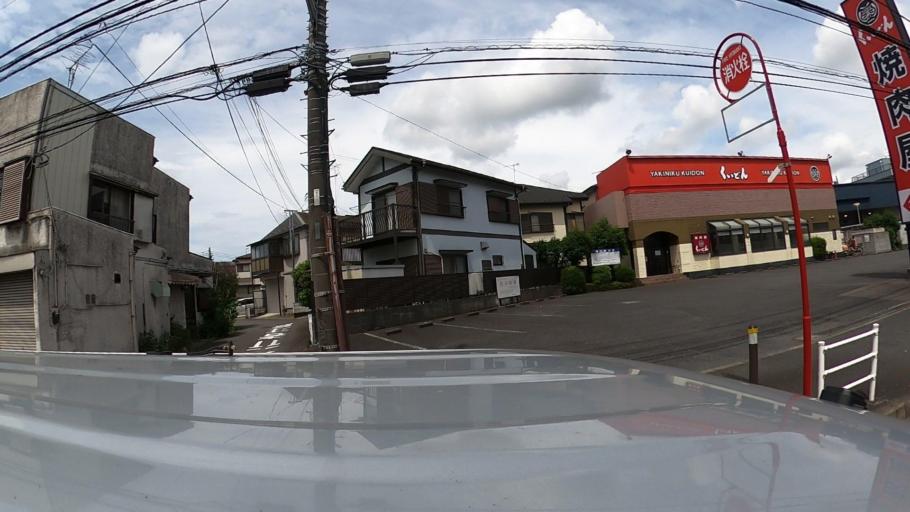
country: JP
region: Kanagawa
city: Fujisawa
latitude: 35.4069
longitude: 139.4699
